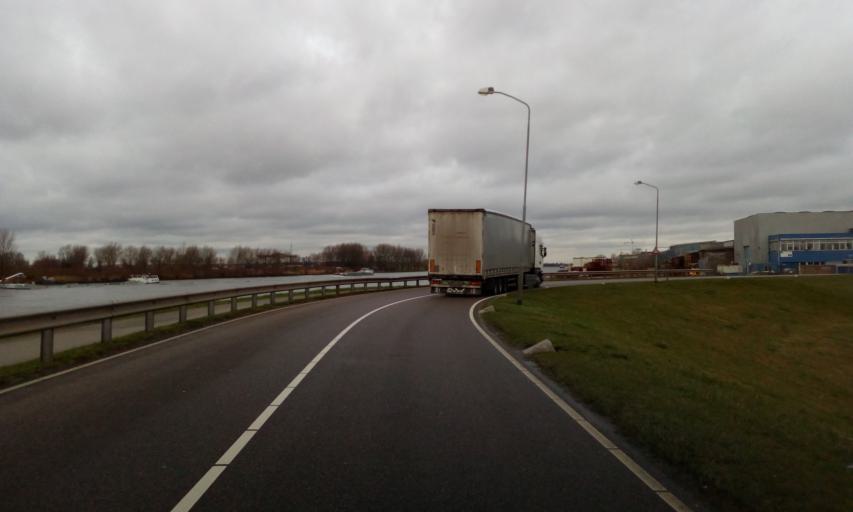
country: NL
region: South Holland
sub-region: Gemeente Alblasserdam
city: Alblasserdam
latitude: 51.8710
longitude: 4.6358
